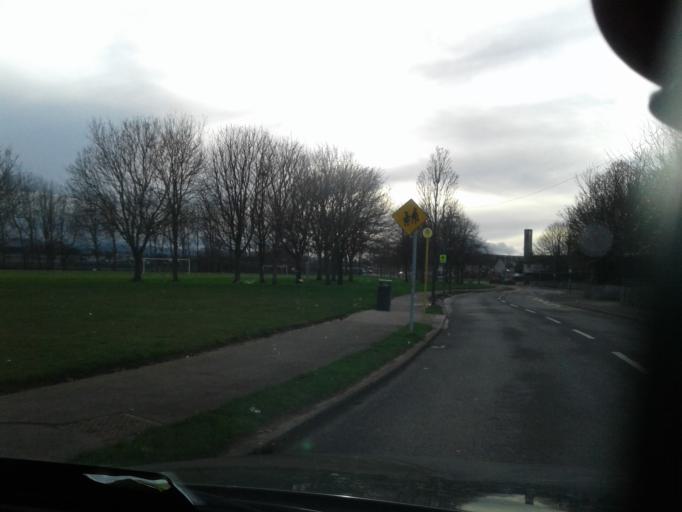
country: IE
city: Coolock
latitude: 53.3845
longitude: -6.1942
